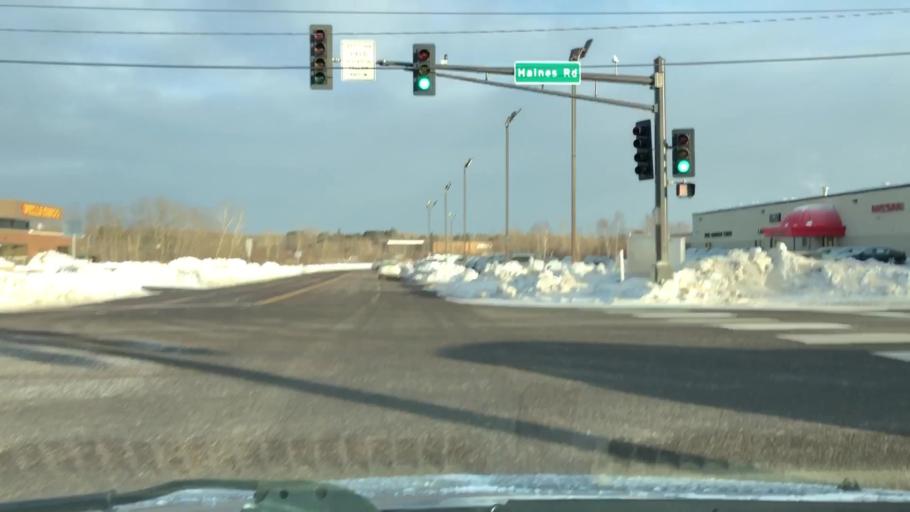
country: US
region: Minnesota
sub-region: Saint Louis County
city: Hermantown
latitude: 46.8130
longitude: -92.1748
